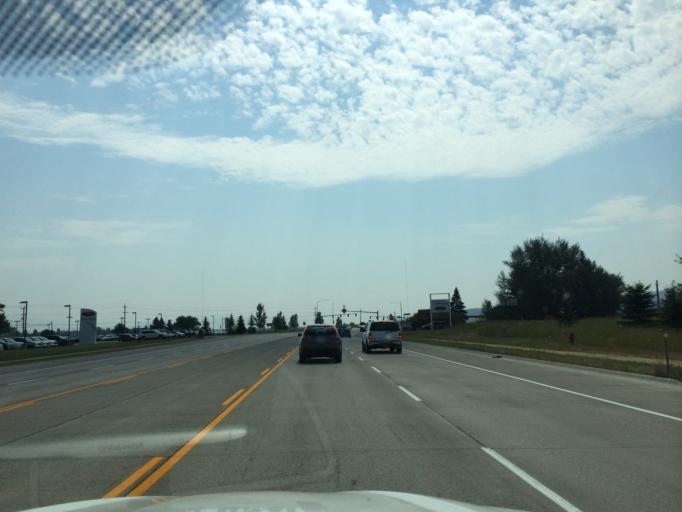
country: US
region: Montana
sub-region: Flathead County
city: Kalispell
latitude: 48.1671
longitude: -114.2903
